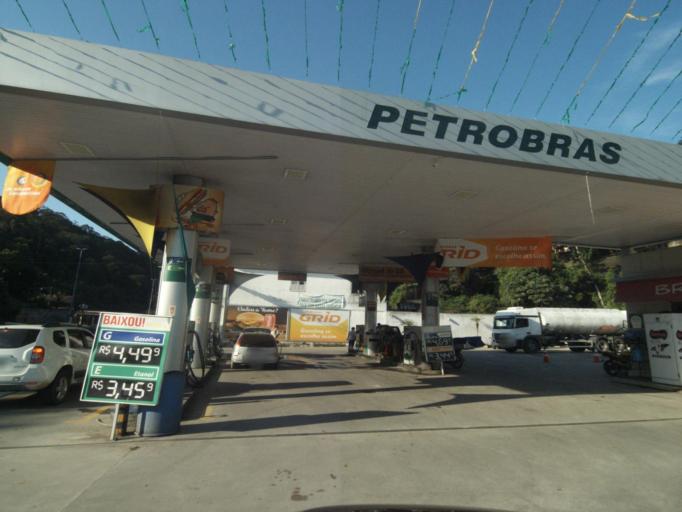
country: BR
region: Rio de Janeiro
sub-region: Sao Goncalo
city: Sao Goncalo
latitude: -22.8763
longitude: -43.0547
